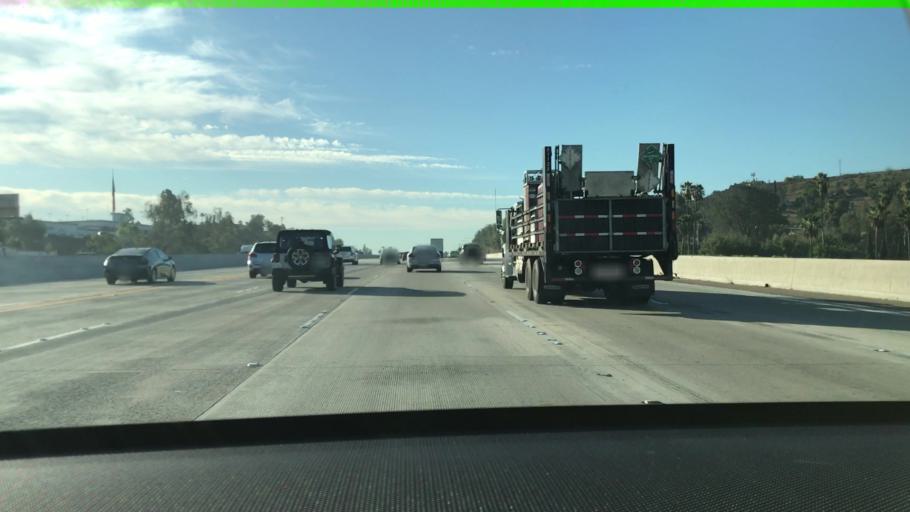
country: US
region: California
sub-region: San Diego County
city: Escondido
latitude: 33.1095
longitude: -117.0958
